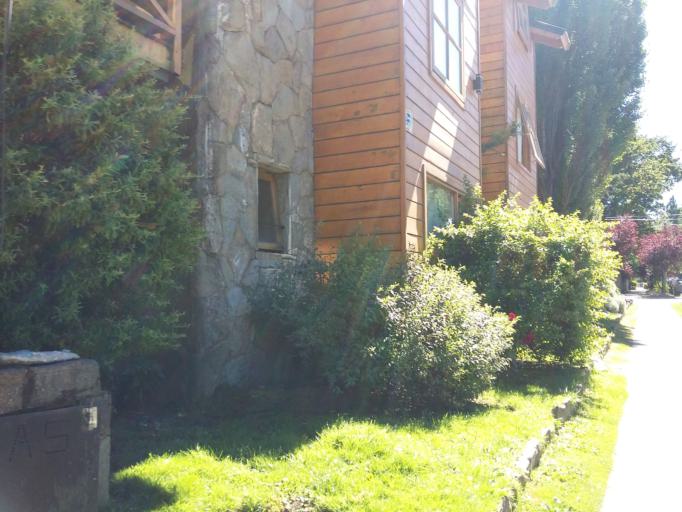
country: AR
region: Neuquen
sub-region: Departamento de Lacar
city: San Martin de los Andes
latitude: -40.1560
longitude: -71.3444
